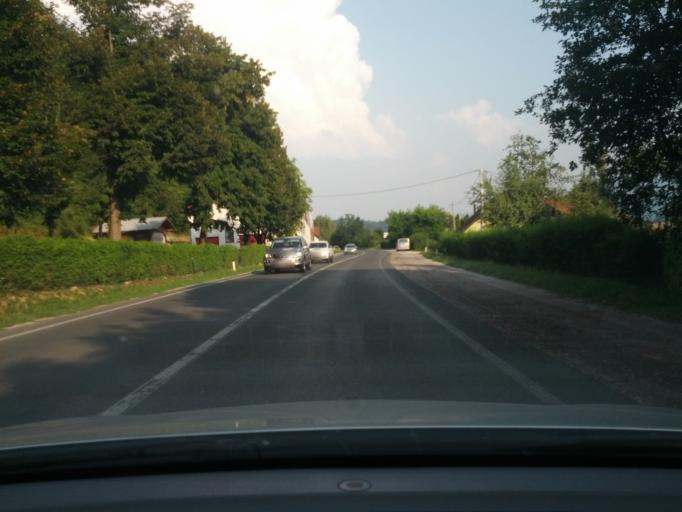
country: SI
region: Log-Dragomer
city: Log pri Brezovici
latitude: 46.0082
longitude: 14.3638
